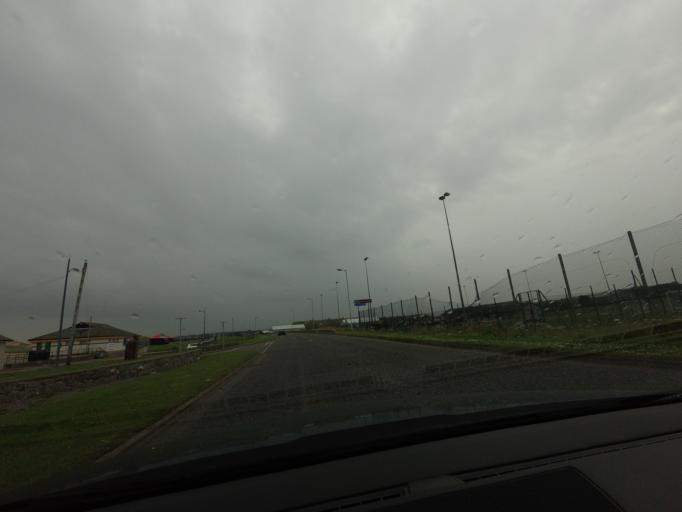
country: GB
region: Scotland
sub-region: Aberdeenshire
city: Fraserburgh
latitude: 57.6851
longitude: -2.0021
